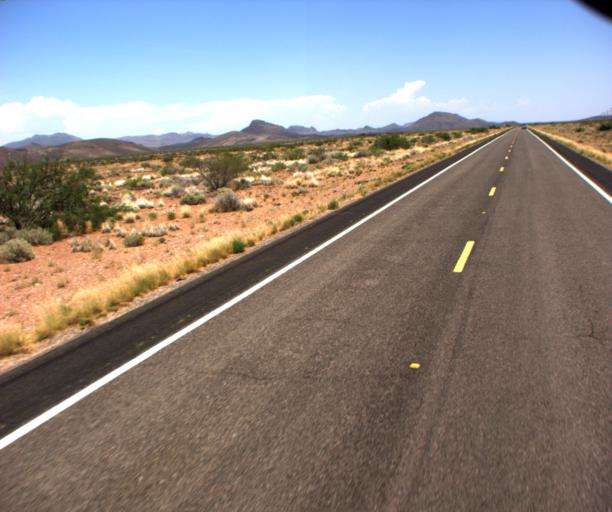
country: US
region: Arizona
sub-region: Graham County
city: Cactus Flat
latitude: 32.7674
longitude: -109.4658
